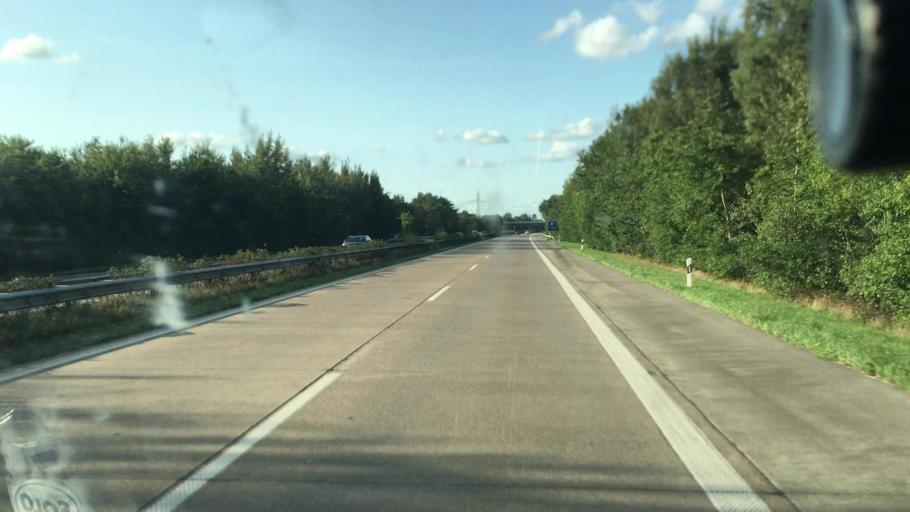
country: DE
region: Lower Saxony
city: Wiefelstede
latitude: 53.3137
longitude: 8.1420
